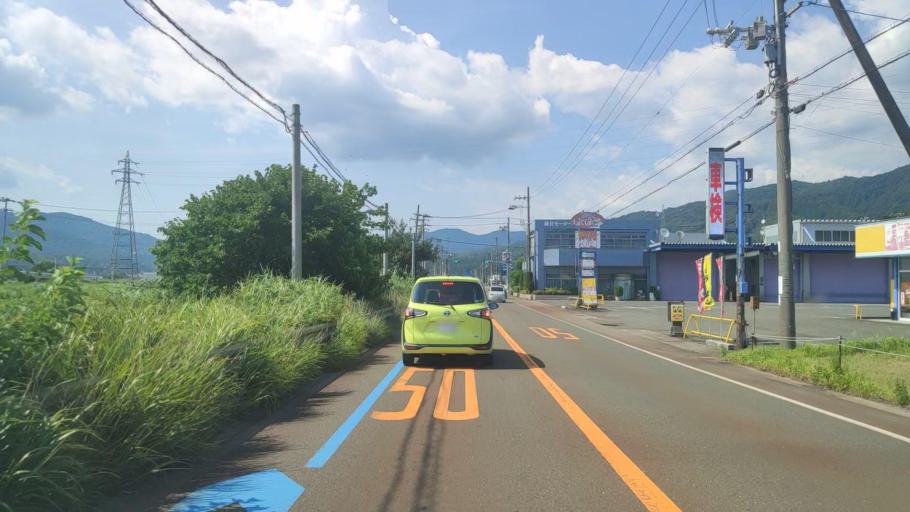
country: JP
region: Fukui
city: Tsuruga
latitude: 35.5172
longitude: 136.1643
